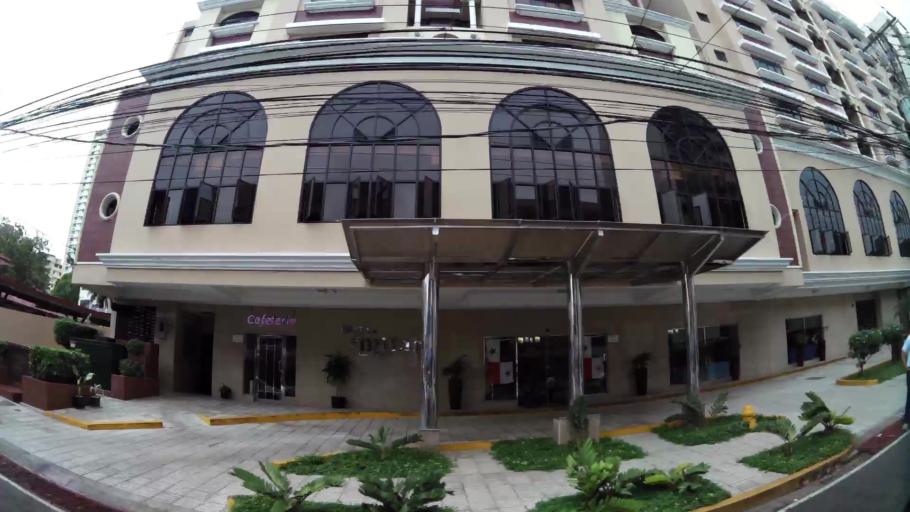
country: PA
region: Panama
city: Panama
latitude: 8.9866
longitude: -79.5273
